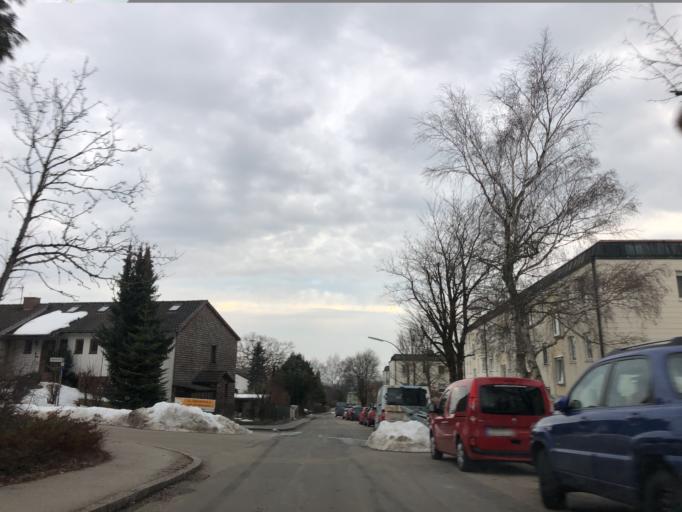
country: DE
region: Bavaria
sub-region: Upper Bavaria
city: Ebersberg
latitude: 48.0726
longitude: 11.9593
